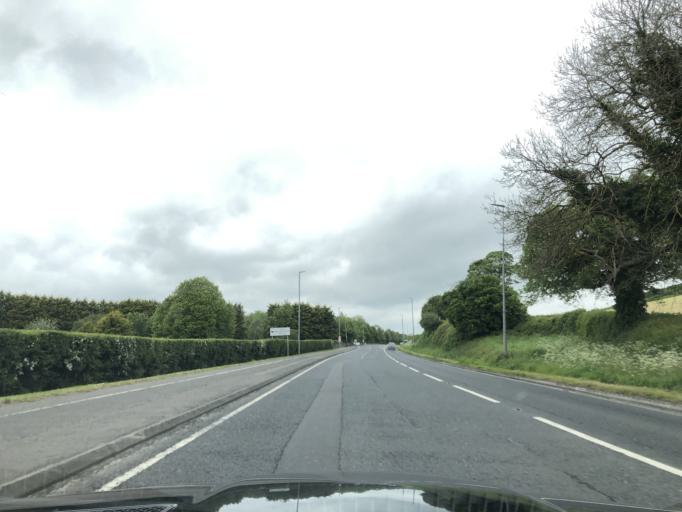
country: GB
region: Northern Ireland
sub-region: Down District
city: Downpatrick
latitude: 54.3425
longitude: -5.7312
